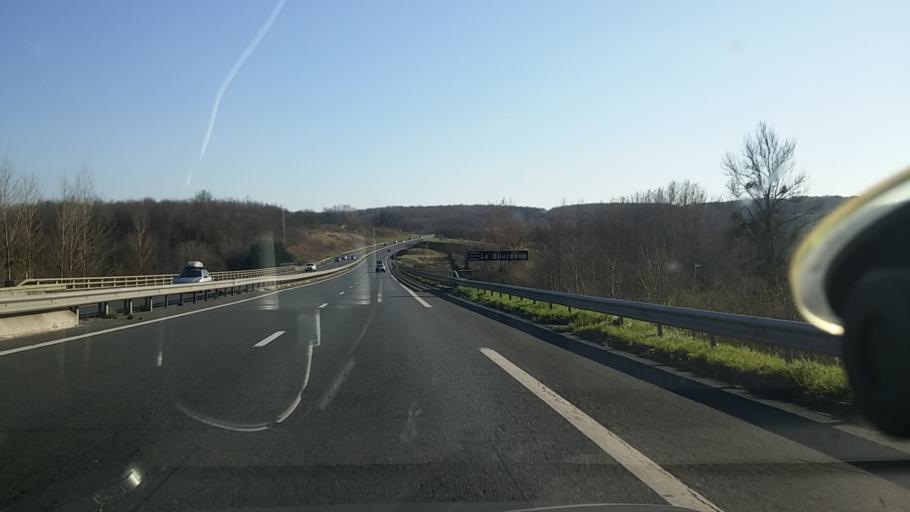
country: FR
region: Centre
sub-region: Departement de l'Indre
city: Saint-Marcel
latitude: 46.6316
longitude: 1.5493
